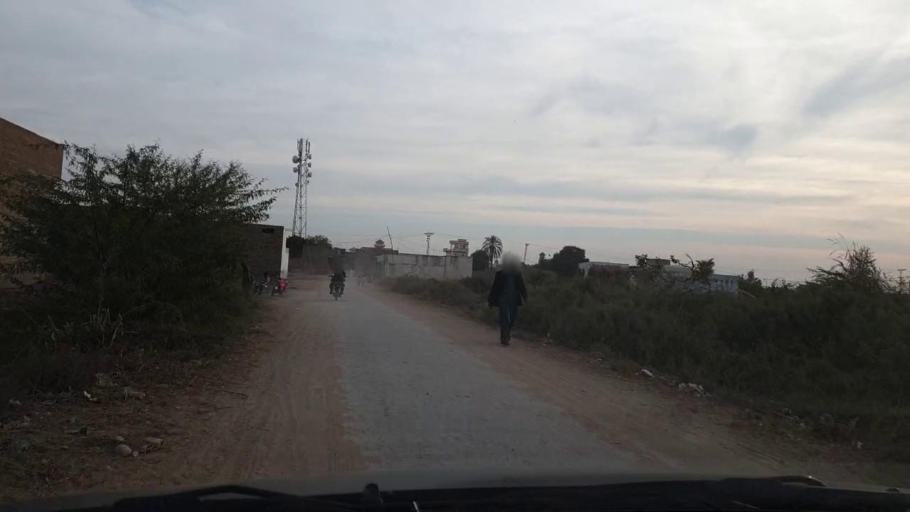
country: PK
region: Sindh
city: Khadro
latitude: 26.1505
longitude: 68.7148
